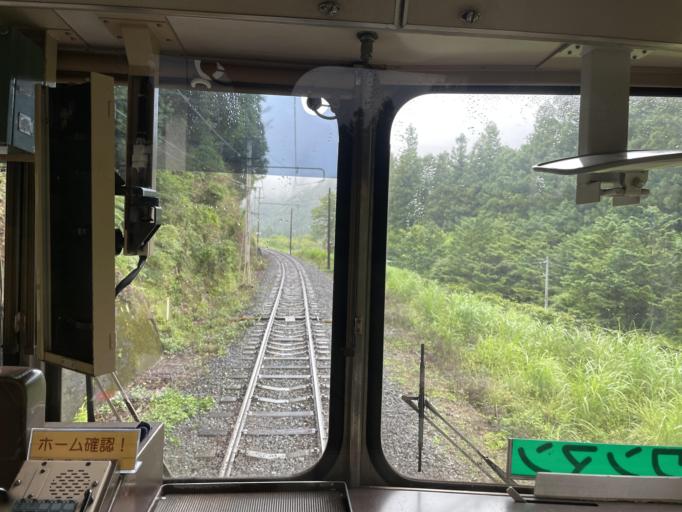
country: JP
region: Saitama
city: Chichibu
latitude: 35.9572
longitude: 139.0030
